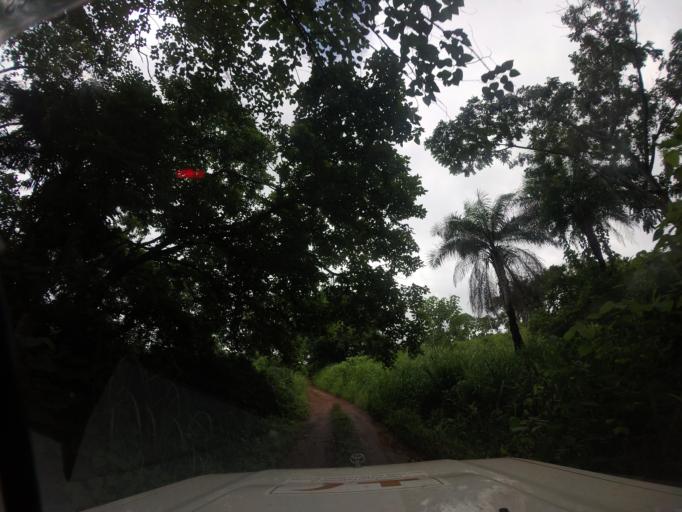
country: SL
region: Northern Province
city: Kamakwie
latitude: 9.6631
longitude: -12.2178
